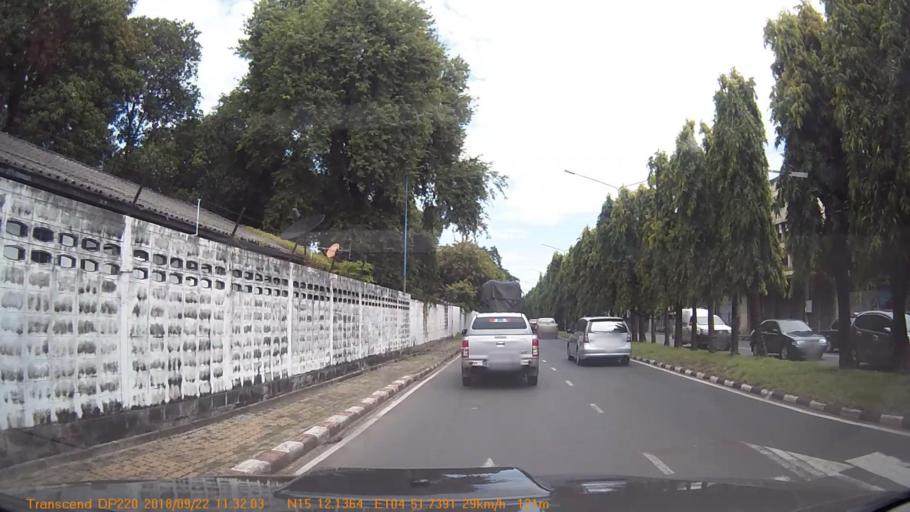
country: TH
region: Changwat Ubon Ratchathani
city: Warin Chamrap
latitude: 15.2023
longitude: 104.8623
